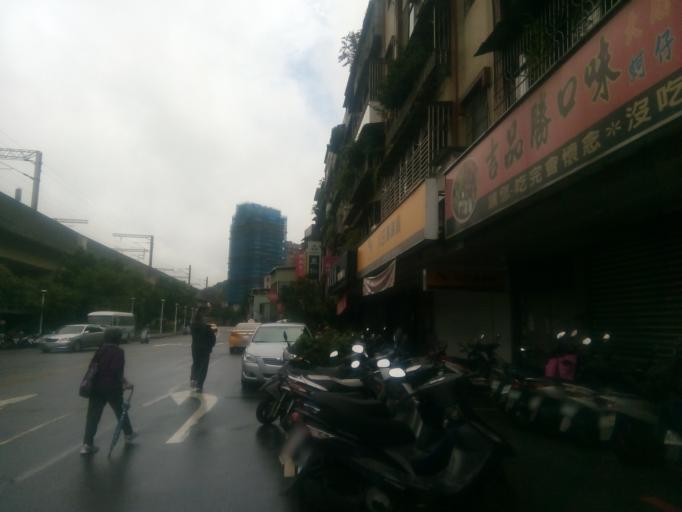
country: TW
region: Taiwan
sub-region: Keelung
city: Keelung
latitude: 25.0690
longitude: 121.6629
